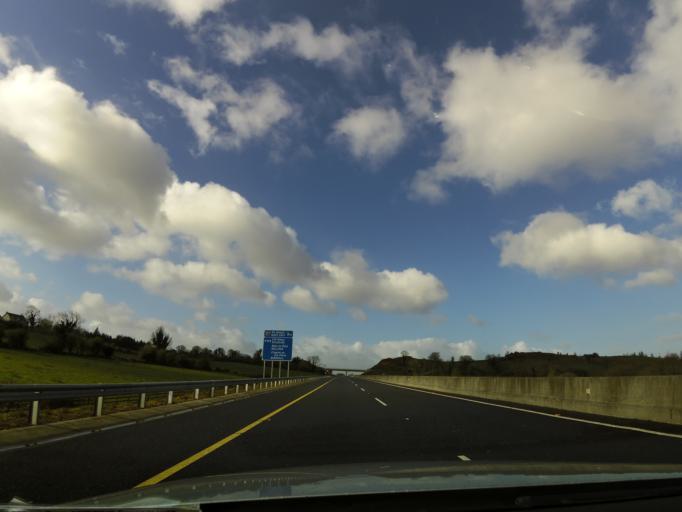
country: IE
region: Munster
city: Ballina
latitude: 52.7743
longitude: -8.3809
